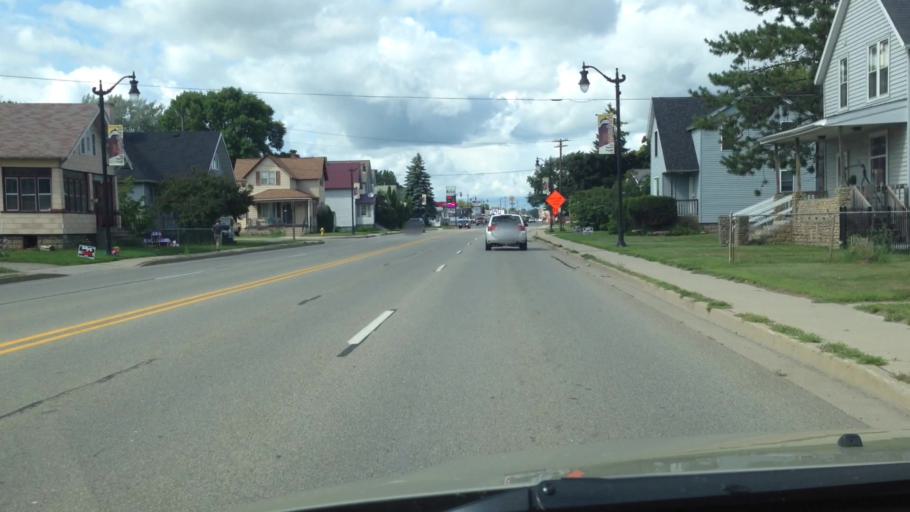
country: US
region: Michigan
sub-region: Menominee County
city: Menominee
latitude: 45.1144
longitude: -87.6142
